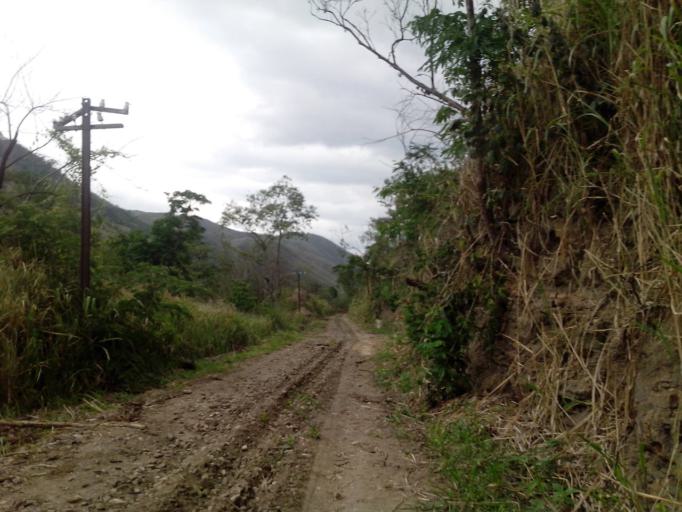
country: BR
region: Rio de Janeiro
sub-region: Miguel Pereira
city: Miguel Pereira
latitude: -22.5045
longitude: -43.5056
